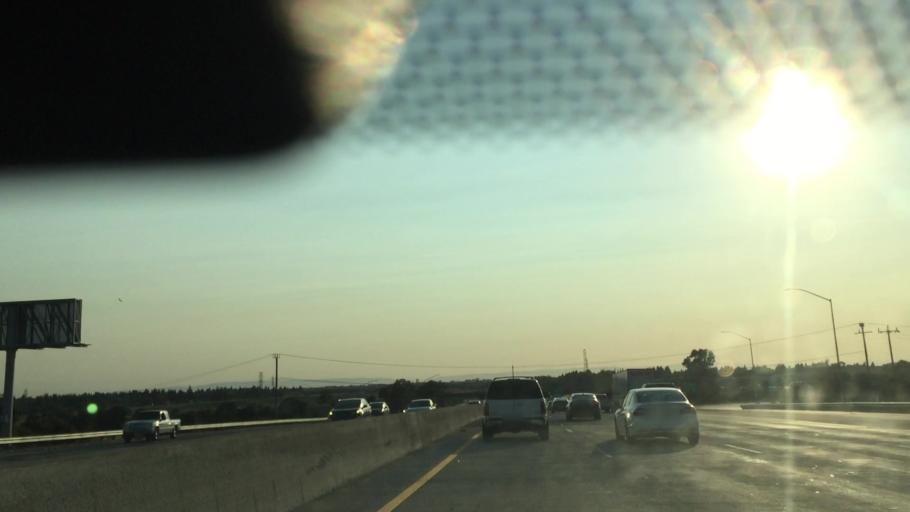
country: US
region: California
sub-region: Sacramento County
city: Rio Linda
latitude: 38.6406
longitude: -121.4747
